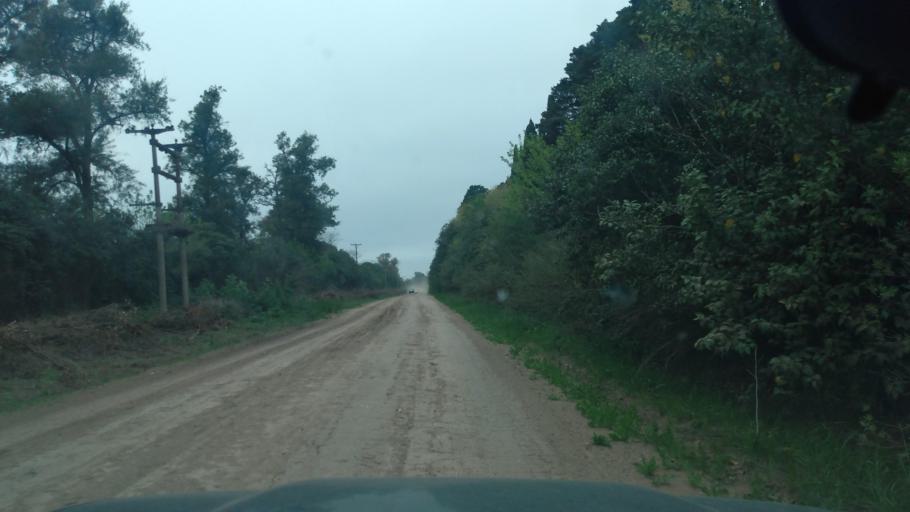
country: AR
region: Buenos Aires
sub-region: Partido de Lujan
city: Lujan
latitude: -34.5428
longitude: -59.2034
